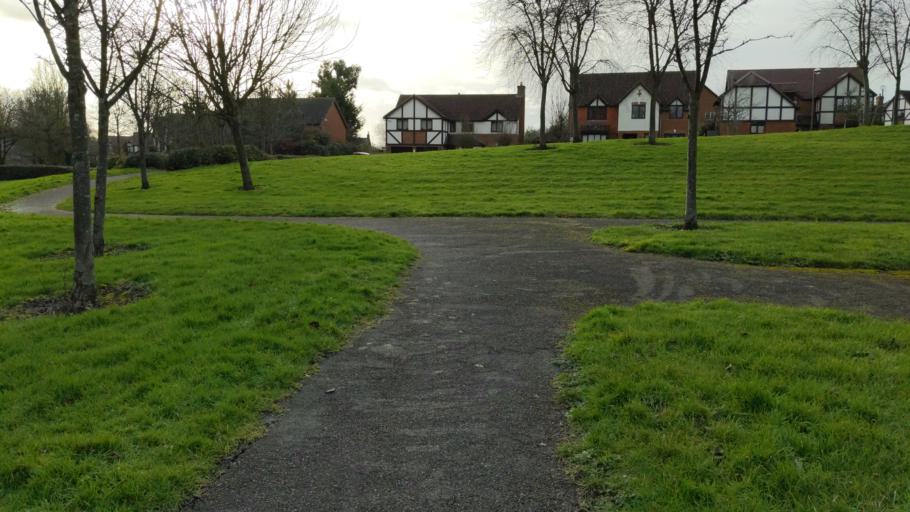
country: GB
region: England
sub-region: Milton Keynes
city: Loughton
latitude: 52.0326
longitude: -0.7766
